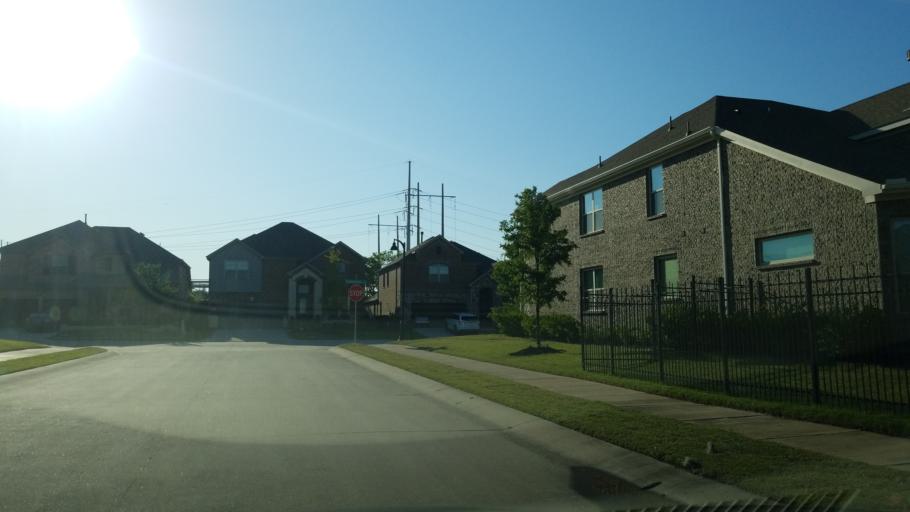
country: US
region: Texas
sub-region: Dallas County
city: Coppell
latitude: 32.9073
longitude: -96.9906
